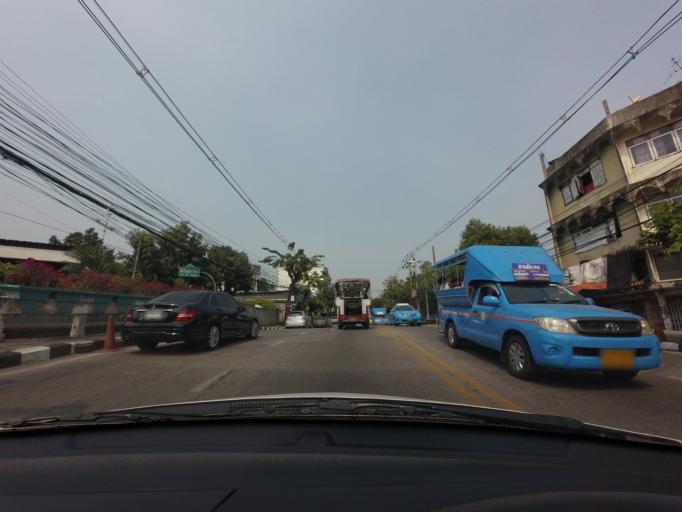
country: TH
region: Bangkok
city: Taling Chan
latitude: 13.7732
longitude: 100.4671
